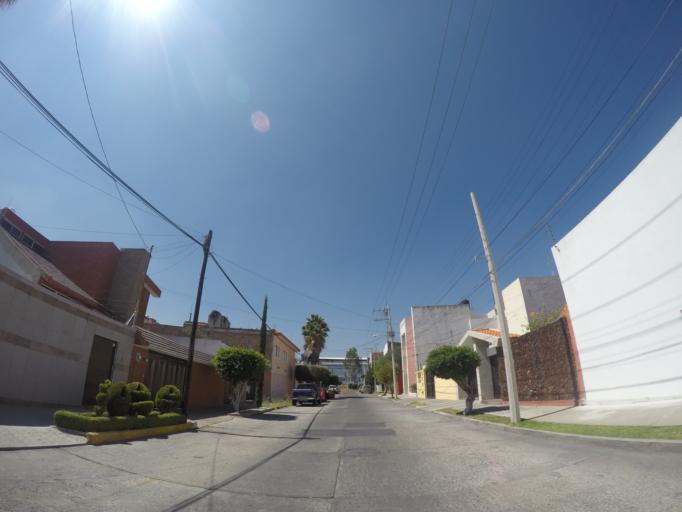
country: MX
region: San Luis Potosi
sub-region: San Luis Potosi
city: San Luis Potosi
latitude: 22.1419
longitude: -101.0080
